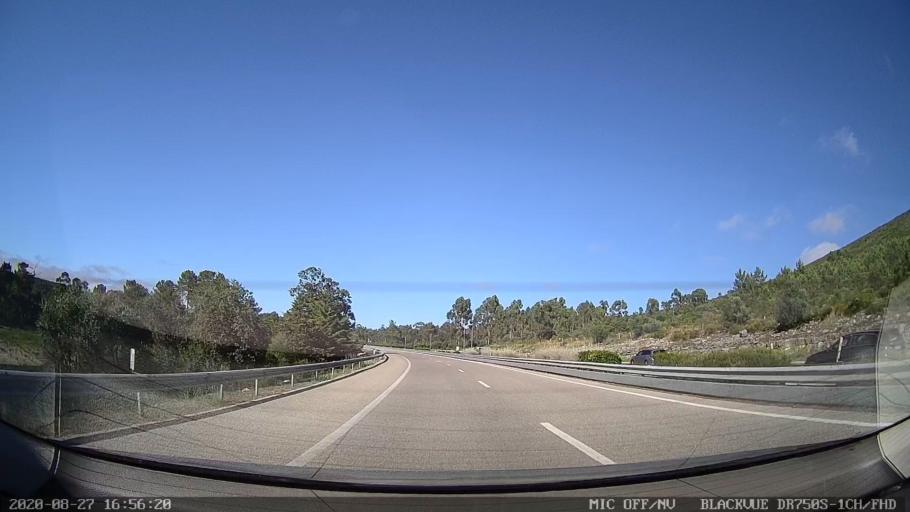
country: PT
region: Santarem
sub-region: Alcanena
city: Alcanena
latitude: 39.5339
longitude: -8.6620
